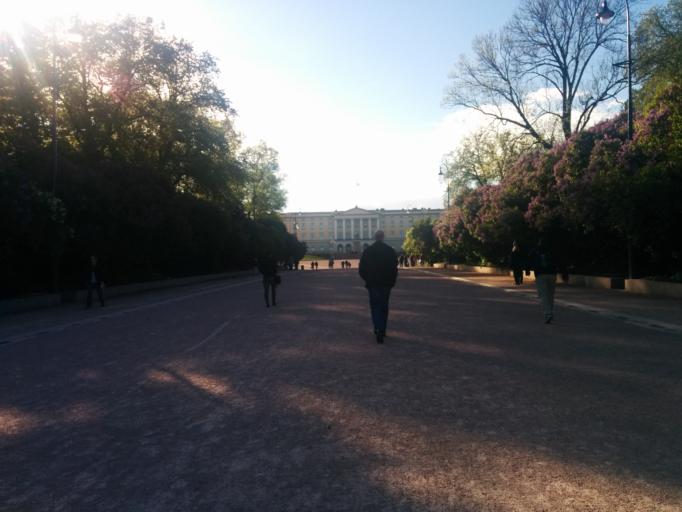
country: NO
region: Oslo
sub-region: Oslo
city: Oslo
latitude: 59.9156
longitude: 10.7325
